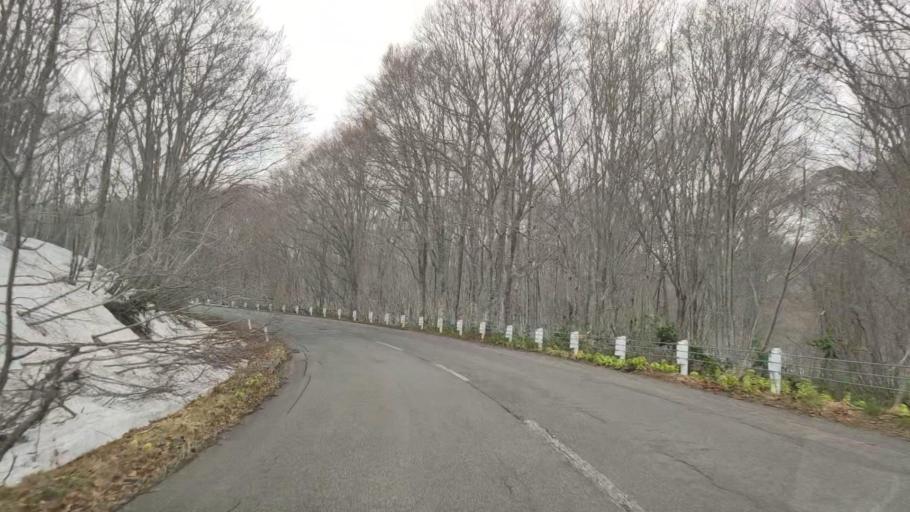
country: JP
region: Aomori
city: Aomori Shi
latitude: 40.6530
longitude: 140.9476
